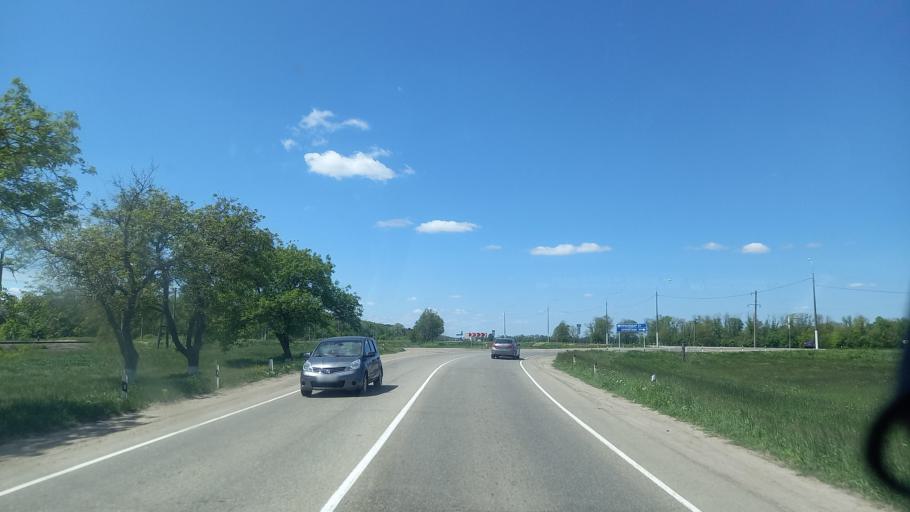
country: RU
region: Krasnodarskiy
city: Tbilisskaya
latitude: 45.3652
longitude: 40.1274
